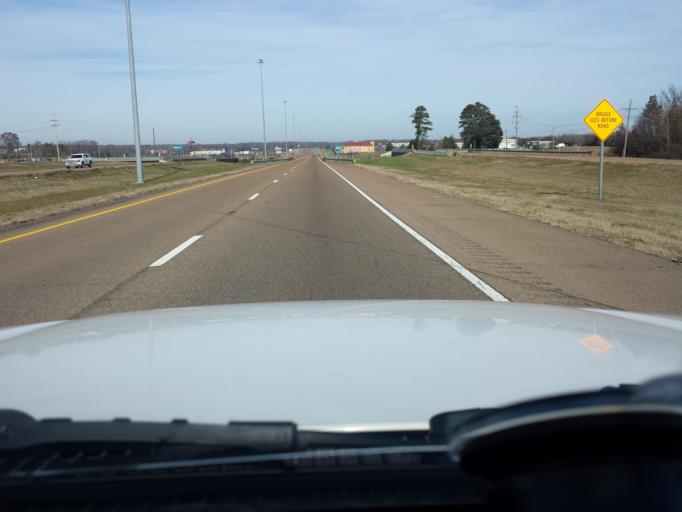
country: US
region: Mississippi
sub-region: Madison County
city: Canton
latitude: 32.5917
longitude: -90.0691
